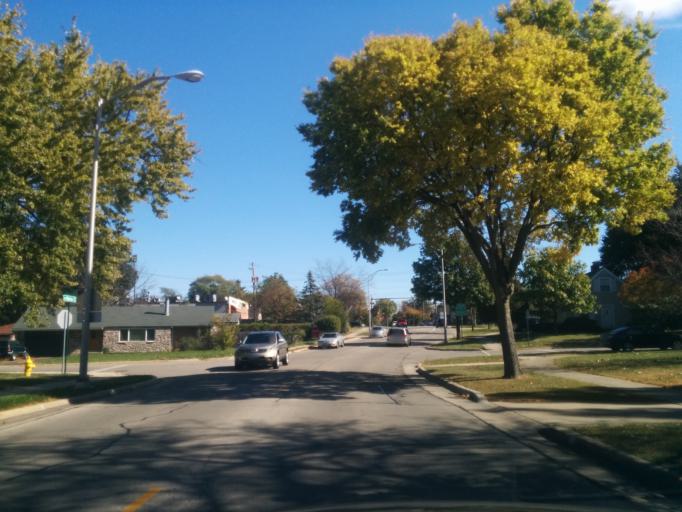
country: US
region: Illinois
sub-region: DuPage County
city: Lombard
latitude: 41.8748
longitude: -88.0198
